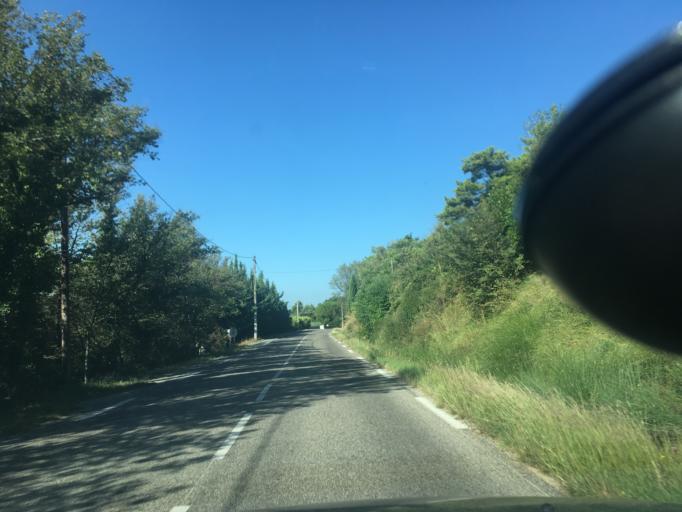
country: FR
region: Provence-Alpes-Cote d'Azur
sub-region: Departement du Var
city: Regusse
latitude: 43.6502
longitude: 6.1641
